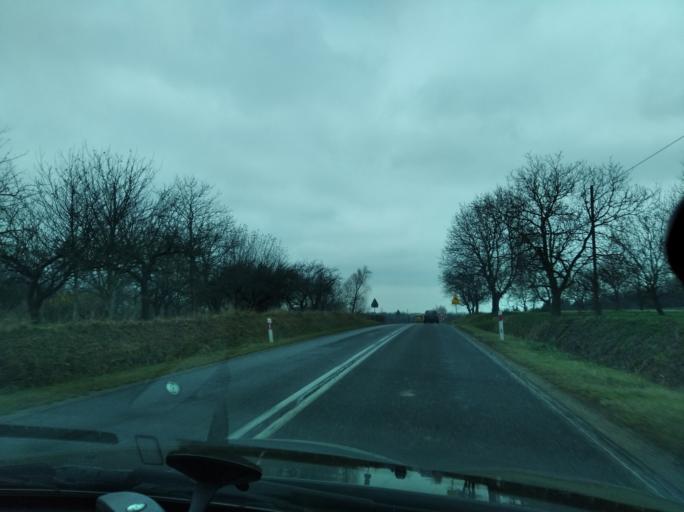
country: PL
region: Subcarpathian Voivodeship
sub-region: Powiat przeworski
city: Sietesz
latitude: 49.9988
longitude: 22.3617
